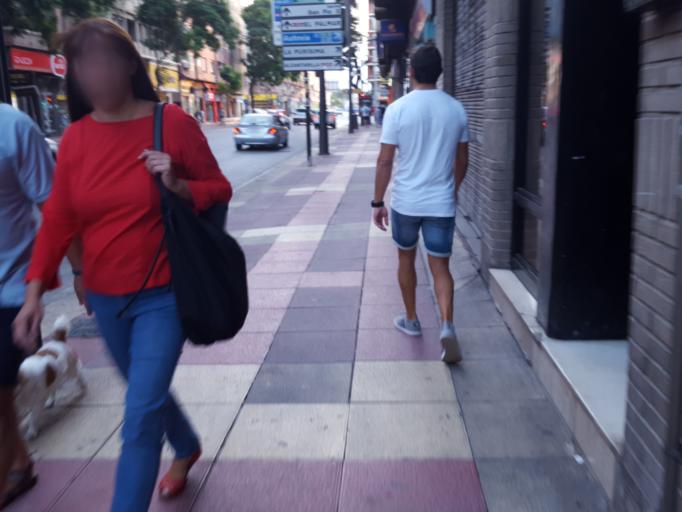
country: ES
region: Murcia
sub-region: Murcia
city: Murcia
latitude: 37.9772
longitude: -1.1324
